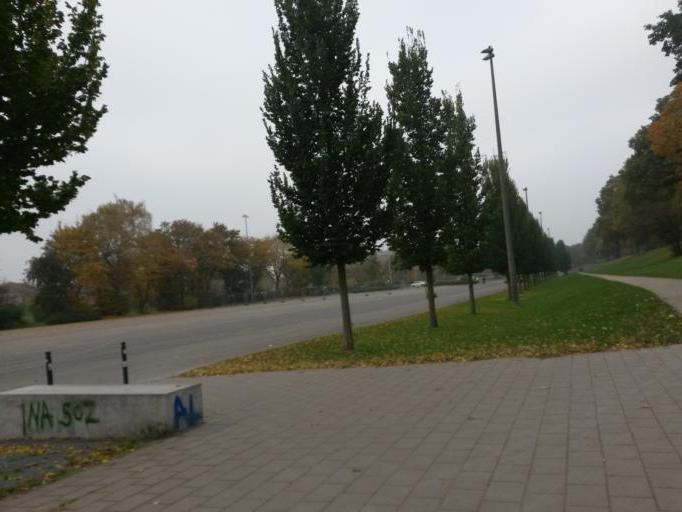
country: DE
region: Bremen
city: Bremen
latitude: 53.0664
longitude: 8.8450
